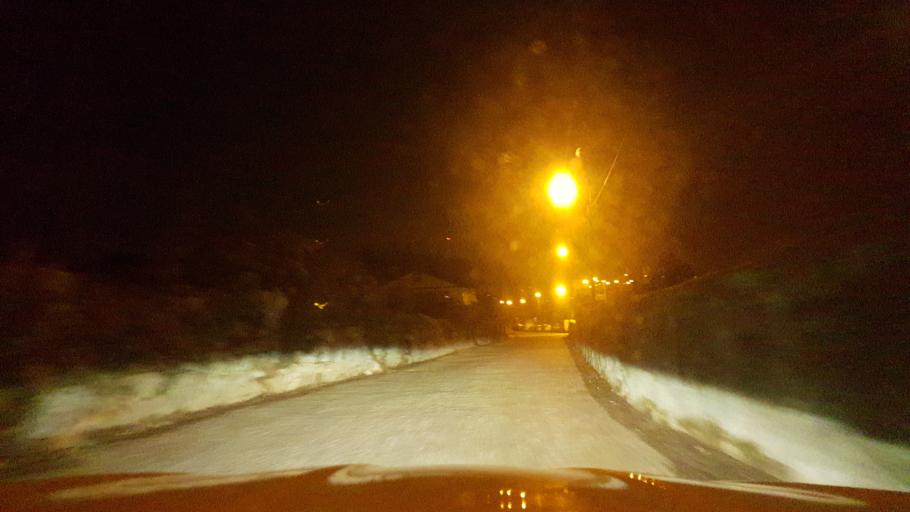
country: PT
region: Porto
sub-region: Matosinhos
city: Guifoes
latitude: 41.2181
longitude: -8.6605
